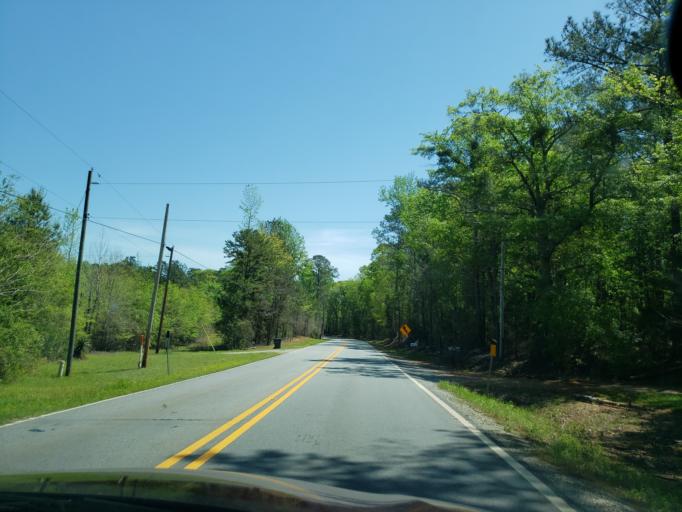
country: US
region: Alabama
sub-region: Tallapoosa County
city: Camp Hill
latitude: 32.6972
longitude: -85.7303
